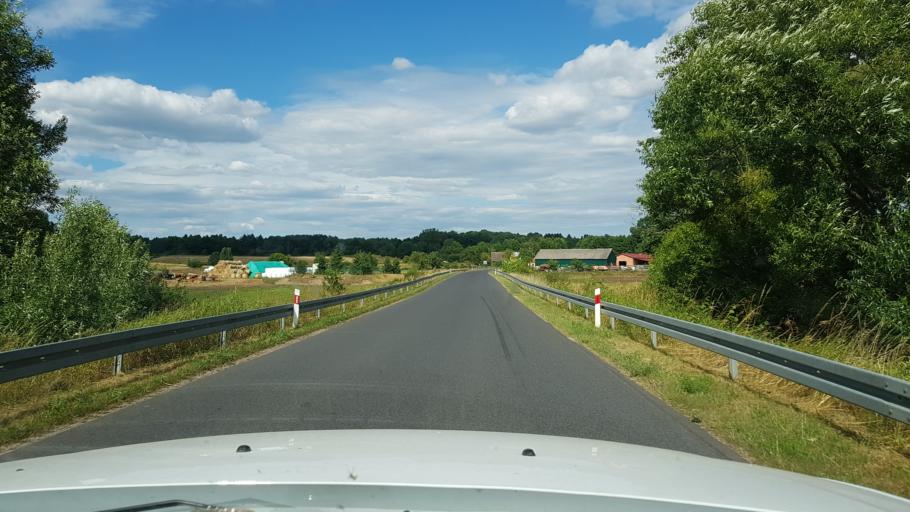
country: PL
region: West Pomeranian Voivodeship
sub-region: Powiat drawski
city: Kalisz Pomorski
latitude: 53.3980
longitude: 15.9639
